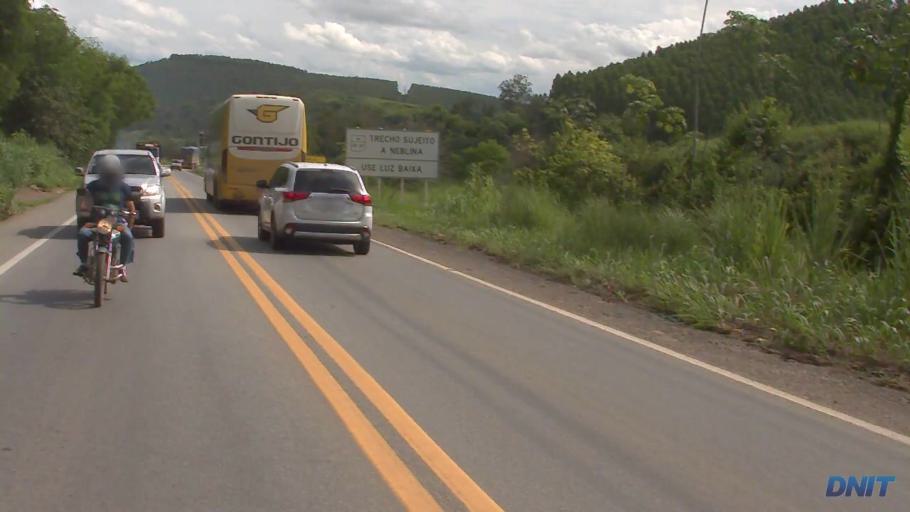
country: BR
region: Minas Gerais
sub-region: Ipaba
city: Ipaba
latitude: -19.3377
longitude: -42.4262
